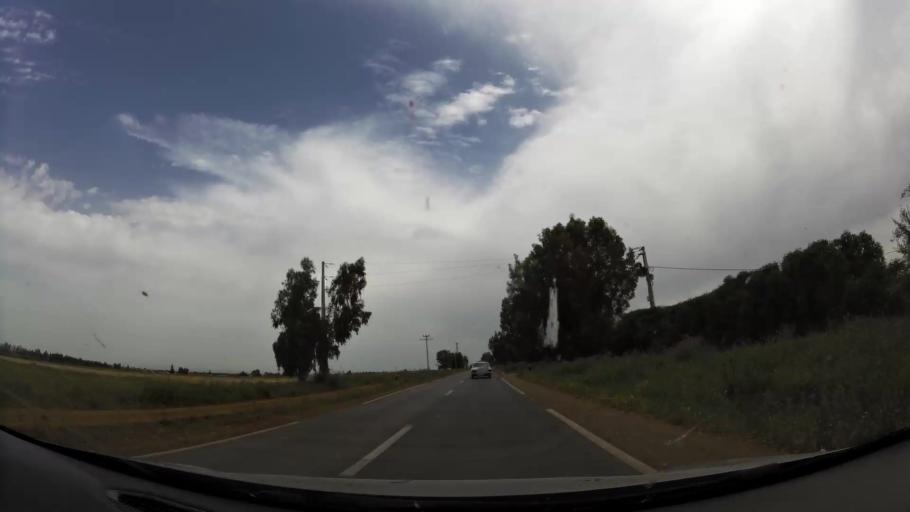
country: MA
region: Rabat-Sale-Zemmour-Zaer
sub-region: Khemisset
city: Tiflet
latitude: 33.8193
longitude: -6.2724
